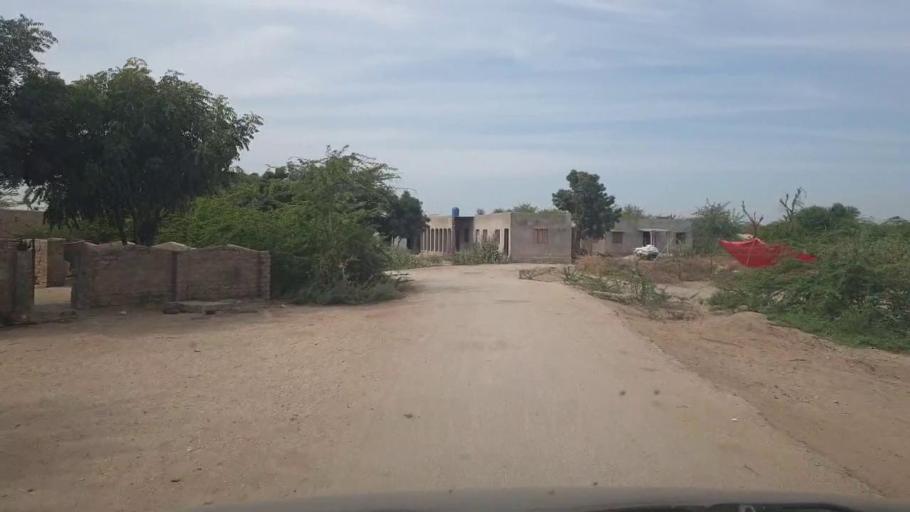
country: PK
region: Sindh
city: Kunri
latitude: 25.2556
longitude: 69.6278
